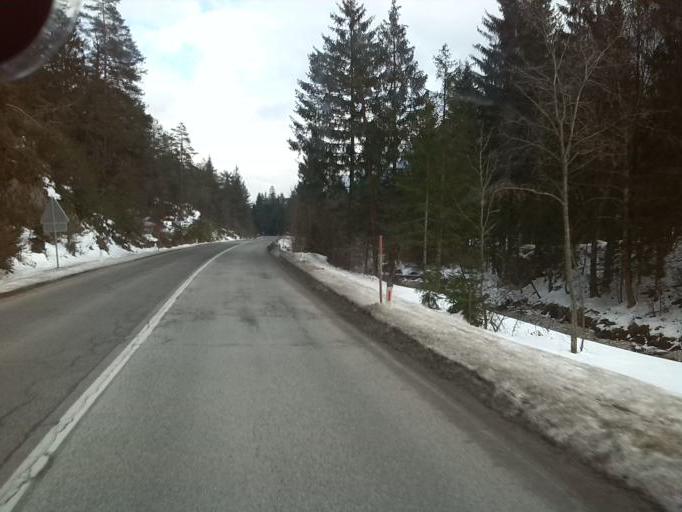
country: SI
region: Kranjska Gora
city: Mojstrana
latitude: 46.4795
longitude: 13.8706
